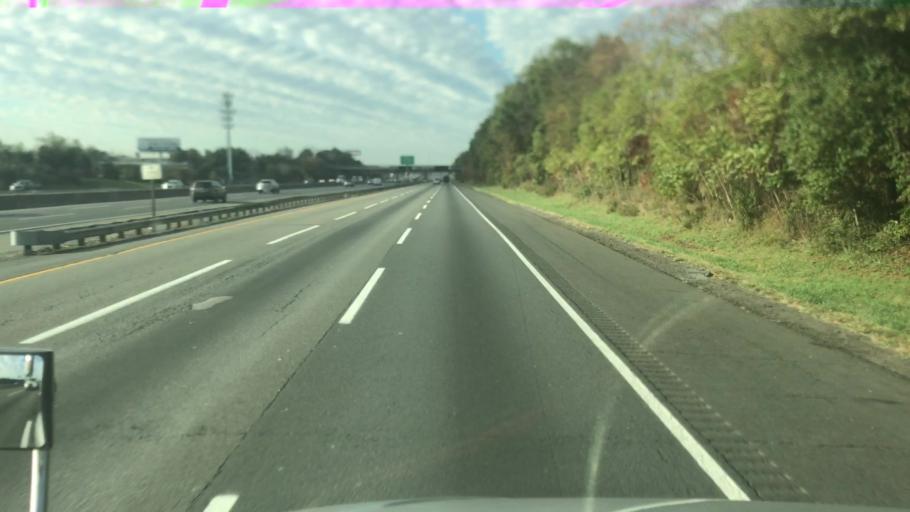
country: US
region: New Jersey
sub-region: Middlesex County
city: Piscataway
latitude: 40.5003
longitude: -74.3834
